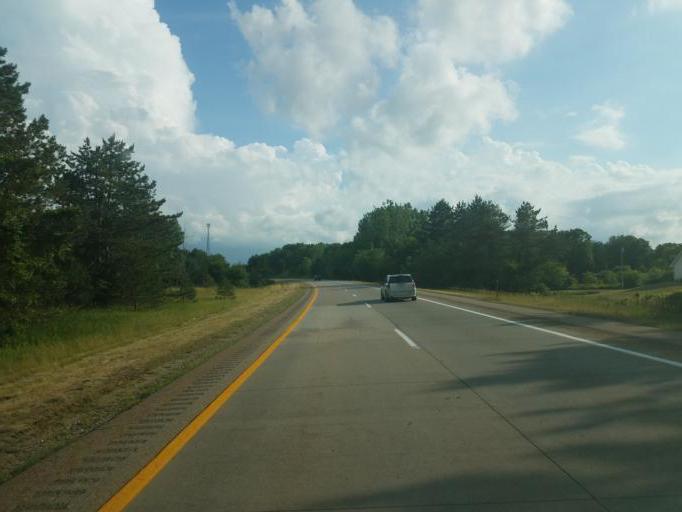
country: US
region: Michigan
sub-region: Calhoun County
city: Marshall
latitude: 42.1648
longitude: -84.9914
